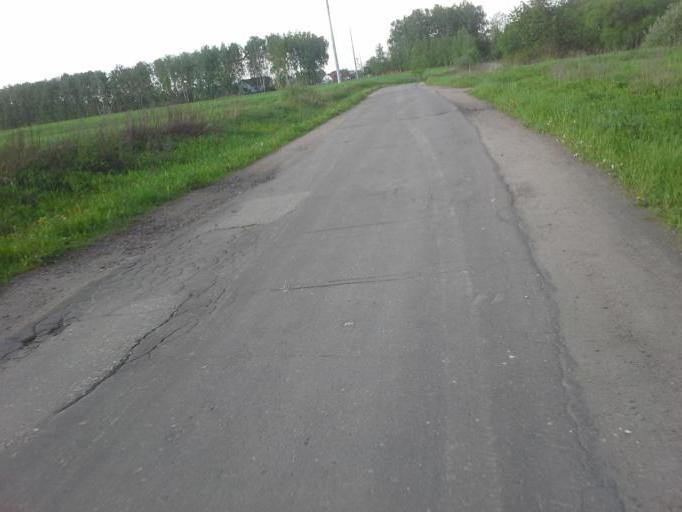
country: RU
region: Moskovskaya
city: Zhavoronki
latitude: 55.6638
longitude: 37.1373
